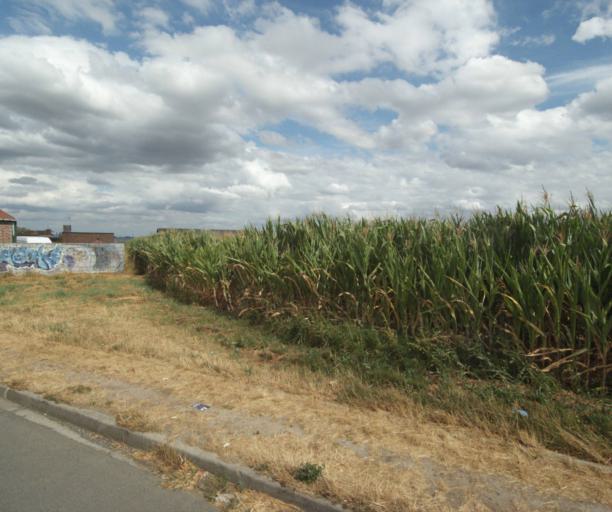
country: FR
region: Nord-Pas-de-Calais
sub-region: Departement du Nord
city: Bousbecque
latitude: 50.7674
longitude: 3.1025
